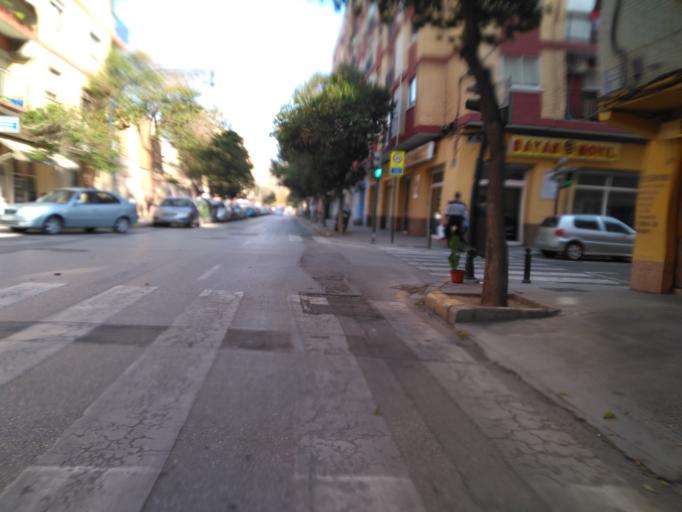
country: ES
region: Valencia
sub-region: Provincia de Valencia
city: Tavernes Blanques
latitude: 39.4924
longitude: -0.3885
